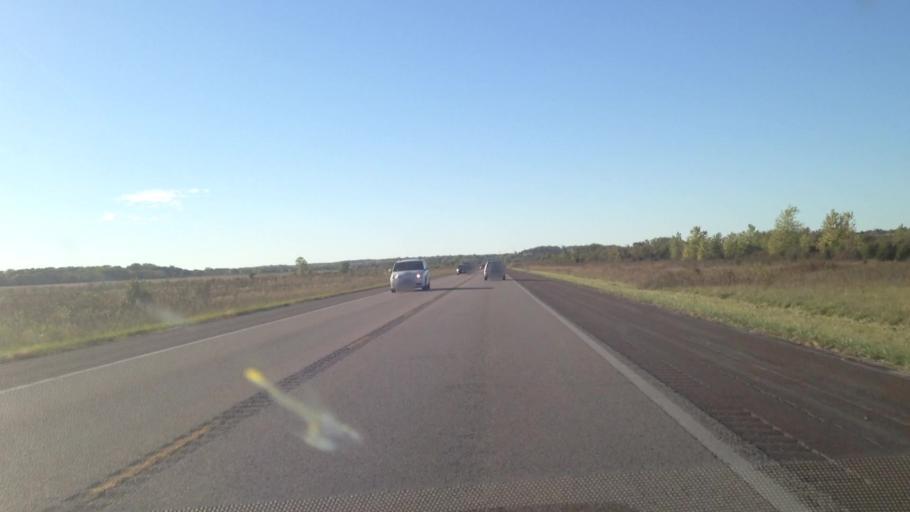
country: US
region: Kansas
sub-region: Douglas County
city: Lawrence
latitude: 38.9260
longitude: -95.2877
